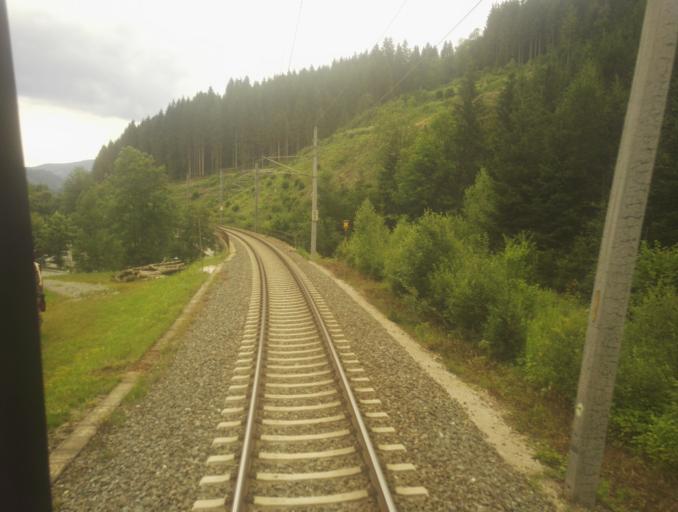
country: AT
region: Salzburg
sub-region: Politischer Bezirk Sankt Johann im Pongau
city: Huttau
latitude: 47.4214
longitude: 13.3414
